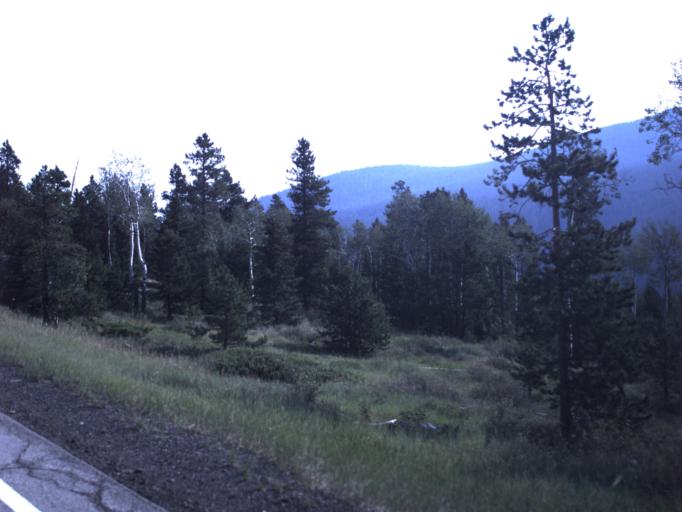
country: US
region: Utah
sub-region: Daggett County
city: Manila
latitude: 40.8377
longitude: -109.4648
